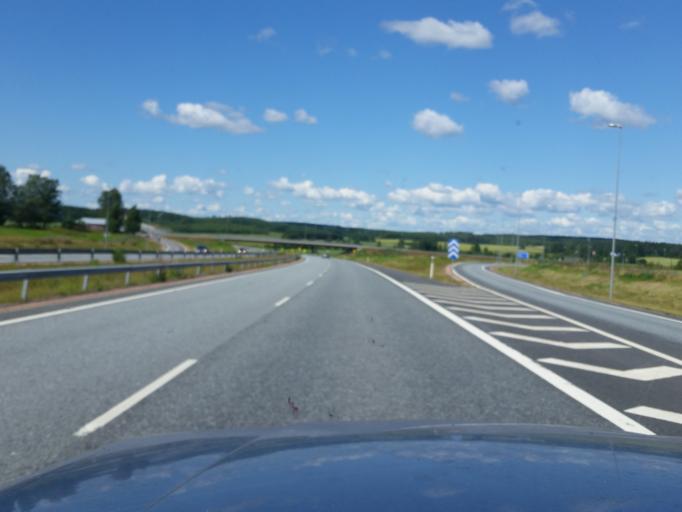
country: FI
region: Varsinais-Suomi
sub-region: Salo
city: Suomusjaervi
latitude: 60.3875
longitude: 23.5921
